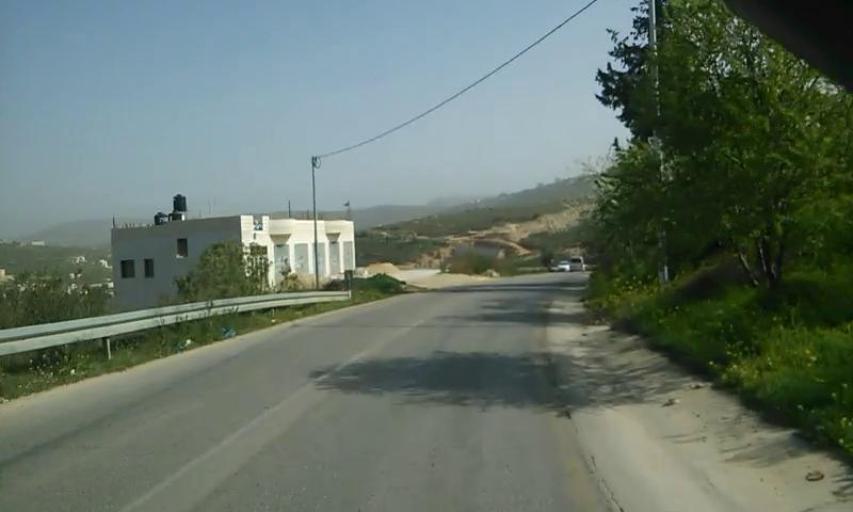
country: PS
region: West Bank
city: Dura al Qar`
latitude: 31.9624
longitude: 35.2252
